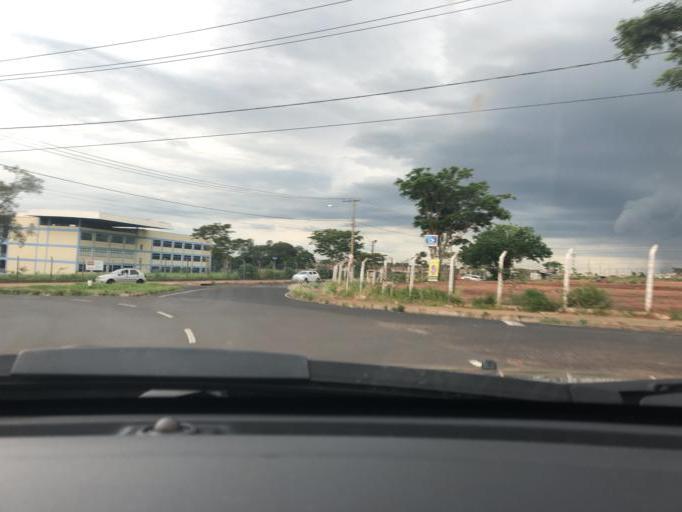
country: BR
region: Sao Paulo
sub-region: Sao Jose Do Rio Preto
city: Sao Jose do Rio Preto
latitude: -20.8420
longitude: -49.4151
